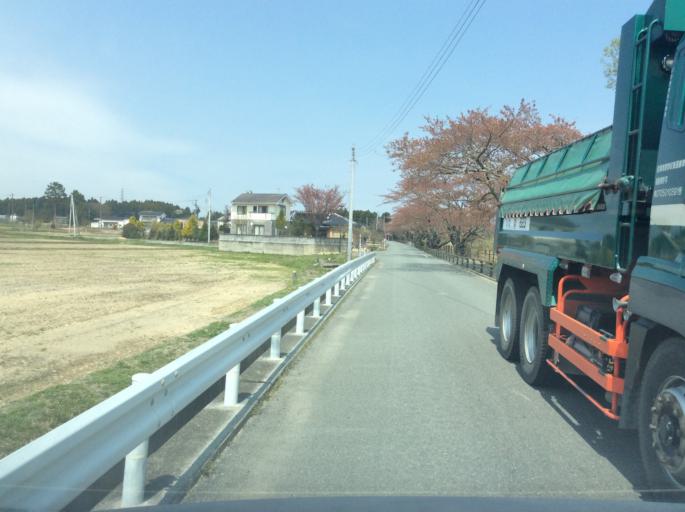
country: JP
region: Fukushima
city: Namie
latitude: 37.3636
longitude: 140.9918
